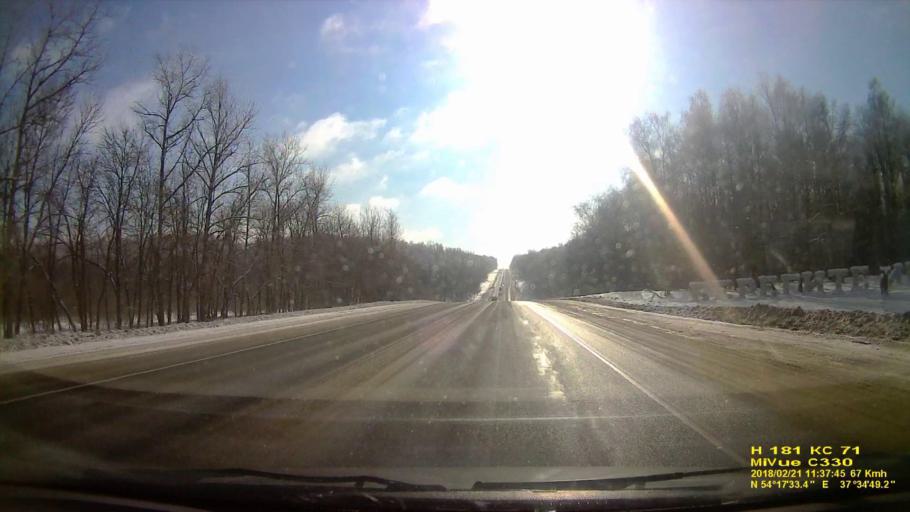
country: RU
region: Tula
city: Gorelki
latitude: 54.2925
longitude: 37.5804
